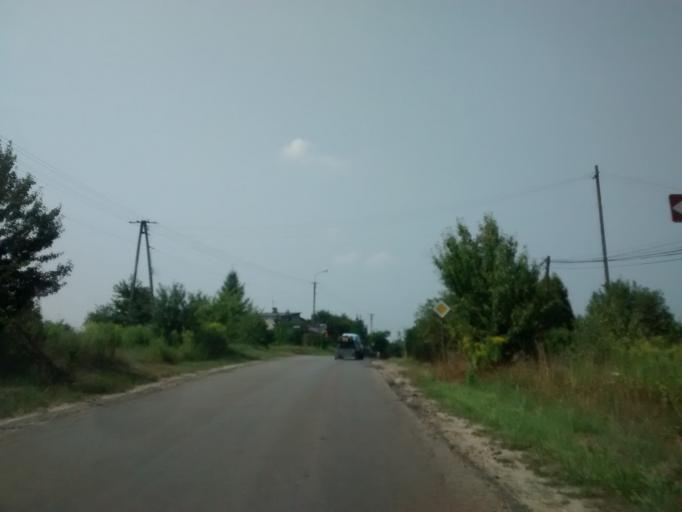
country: PL
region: Lesser Poland Voivodeship
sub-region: Powiat olkuski
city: Klucze
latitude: 50.3667
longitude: 19.5246
